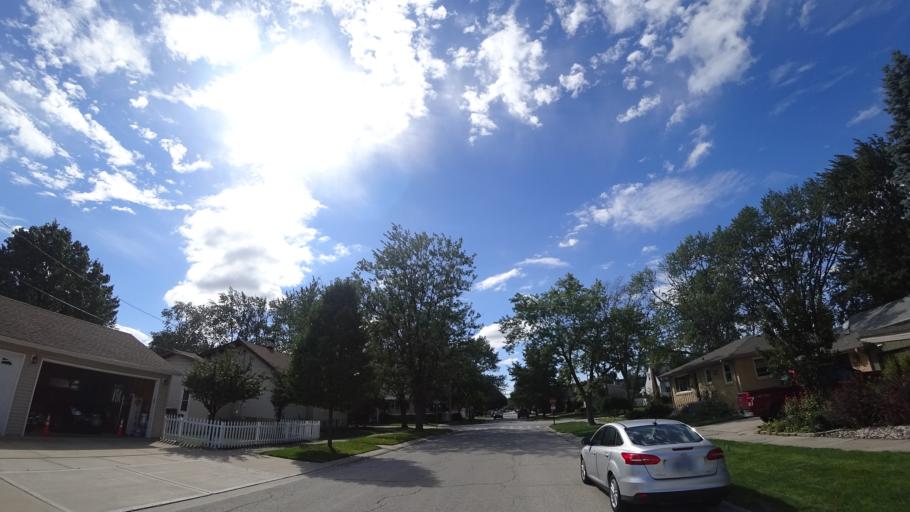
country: US
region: Illinois
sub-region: Cook County
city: Oak Lawn
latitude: 41.7216
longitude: -87.7573
